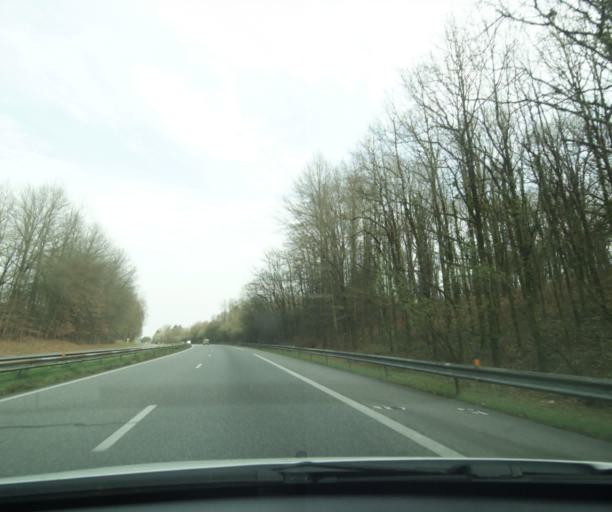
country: FR
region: Aquitaine
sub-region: Departement des Pyrenees-Atlantiques
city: Orthez
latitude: 43.4764
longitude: -0.7892
